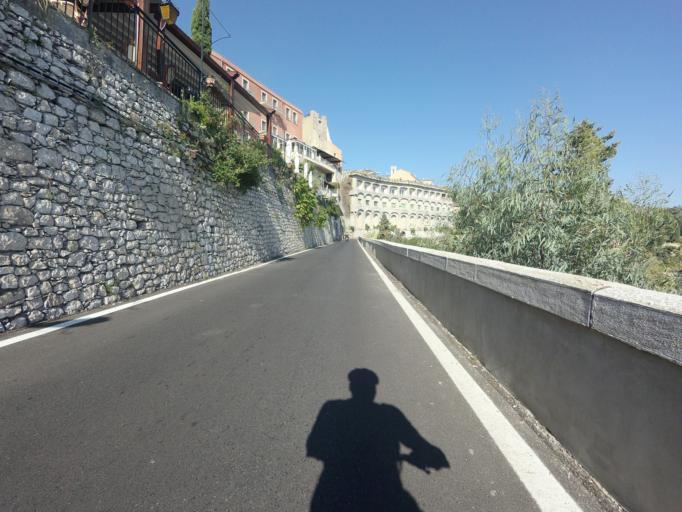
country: IT
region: Sicily
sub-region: Messina
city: Taormina
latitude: 37.8509
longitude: 15.2849
